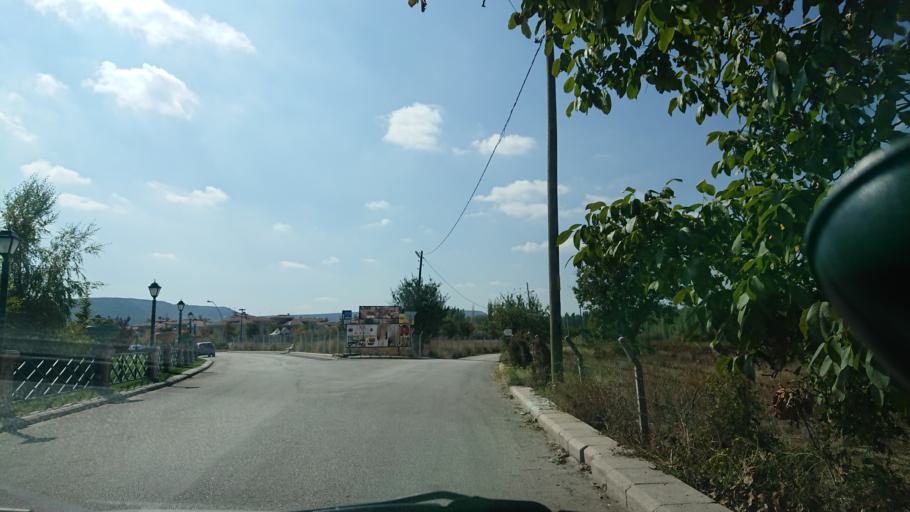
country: TR
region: Eskisehir
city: Eskisehir
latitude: 39.7574
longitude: 30.4797
